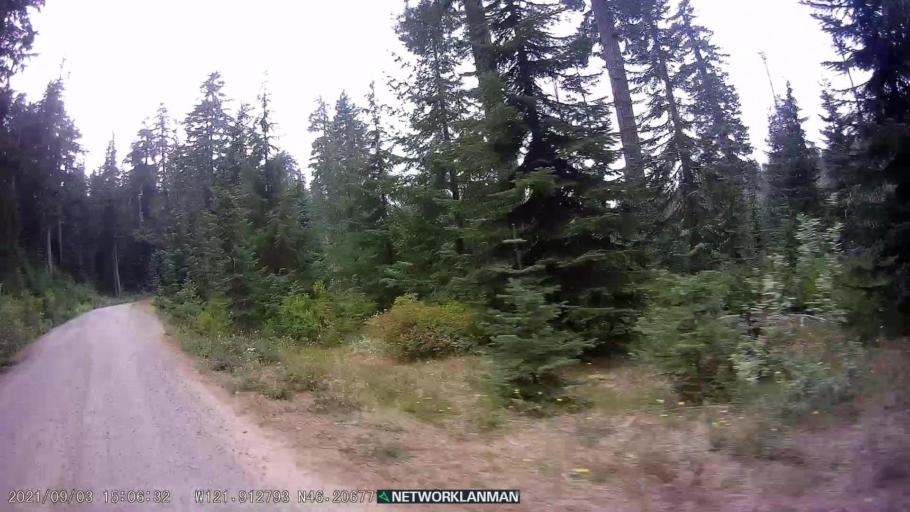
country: US
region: Washington
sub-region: Skamania County
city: Carson
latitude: 46.2065
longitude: -121.9125
